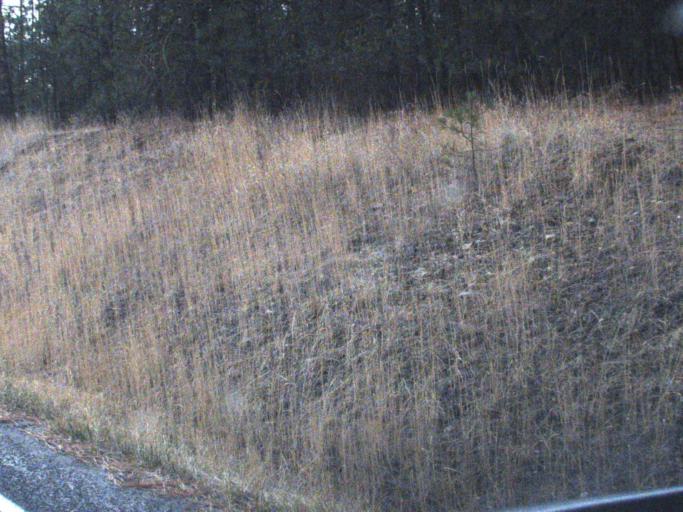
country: US
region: Washington
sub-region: Lincoln County
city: Davenport
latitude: 47.9951
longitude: -118.2822
